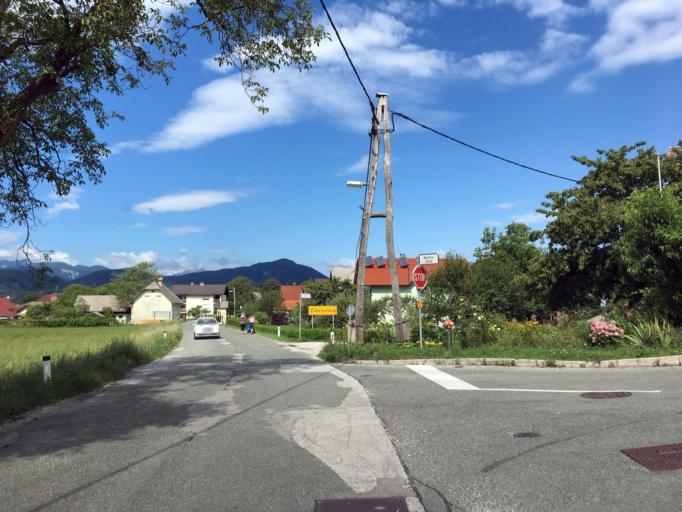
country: SI
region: Zirovnica
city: Zirovnica
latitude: 46.3963
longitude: 14.1511
